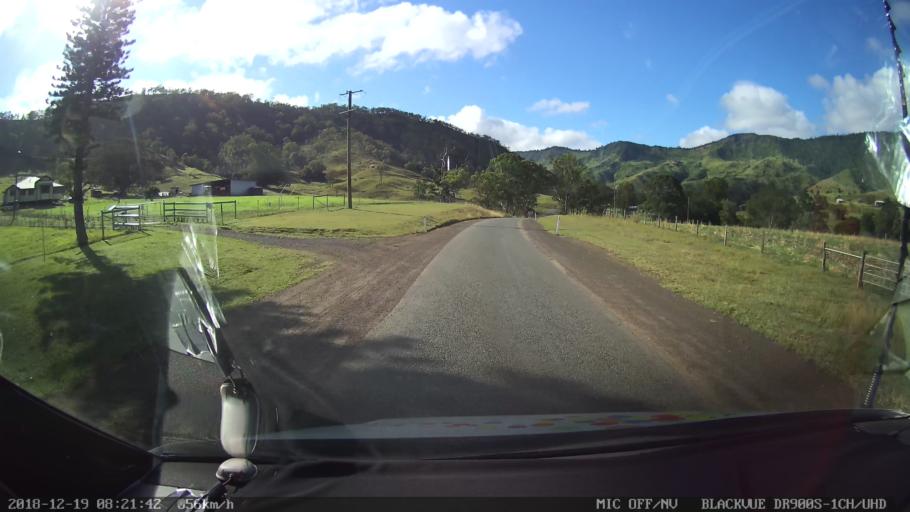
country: AU
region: New South Wales
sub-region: Kyogle
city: Kyogle
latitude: -28.2991
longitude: 152.9106
